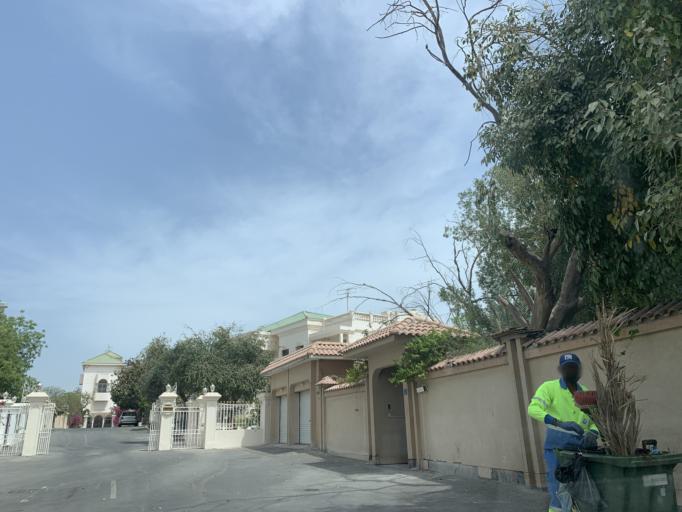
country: BH
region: Northern
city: Ar Rifa'
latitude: 26.1434
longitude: 50.5597
